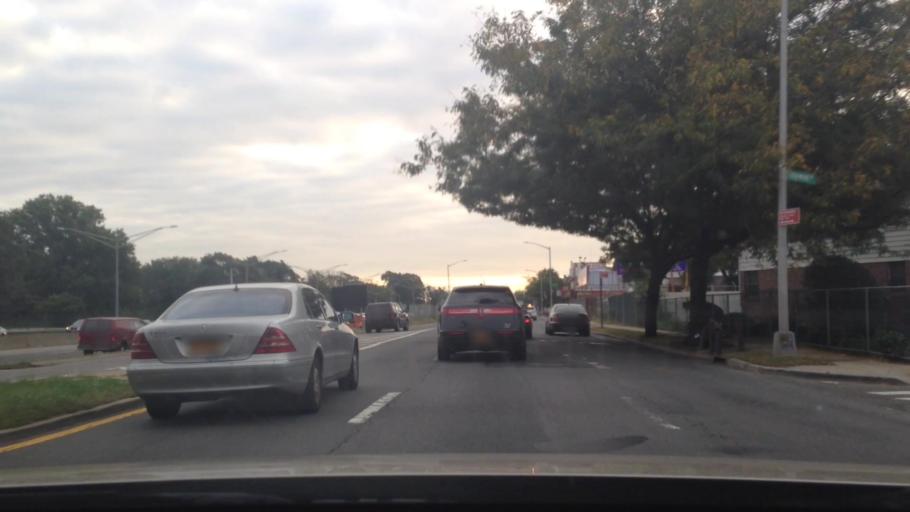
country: US
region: New York
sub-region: Nassau County
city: South Valley Stream
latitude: 40.6655
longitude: -73.7489
